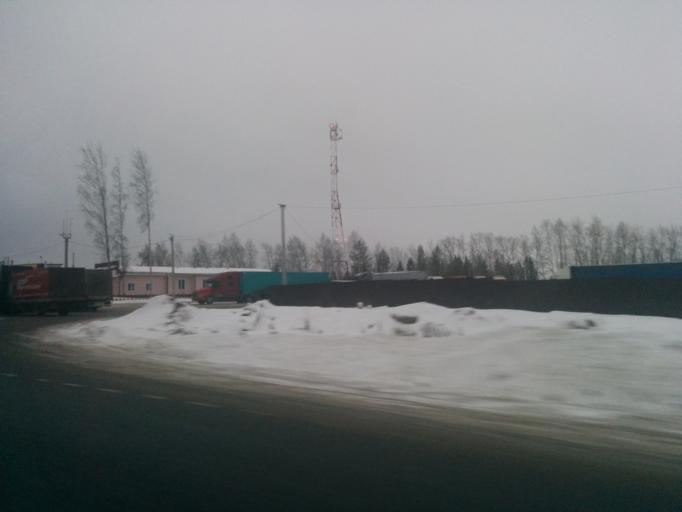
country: RU
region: Perm
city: Nytva
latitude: 57.9796
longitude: 55.3086
